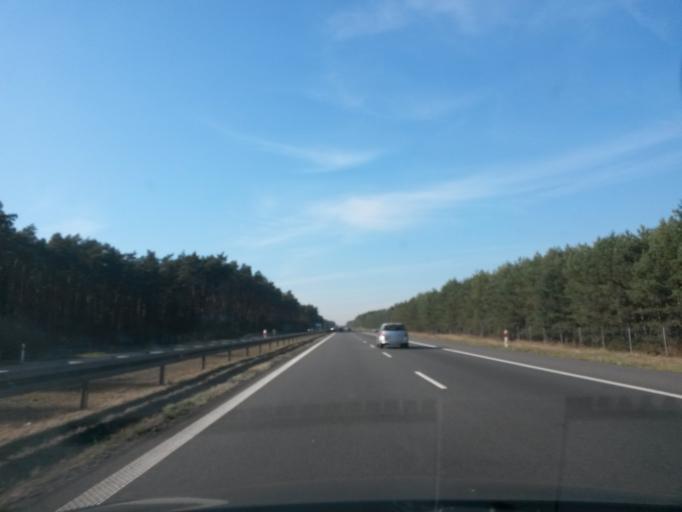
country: PL
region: Opole Voivodeship
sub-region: Powiat opolski
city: Komprachcice
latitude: 50.6066
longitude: 17.7837
